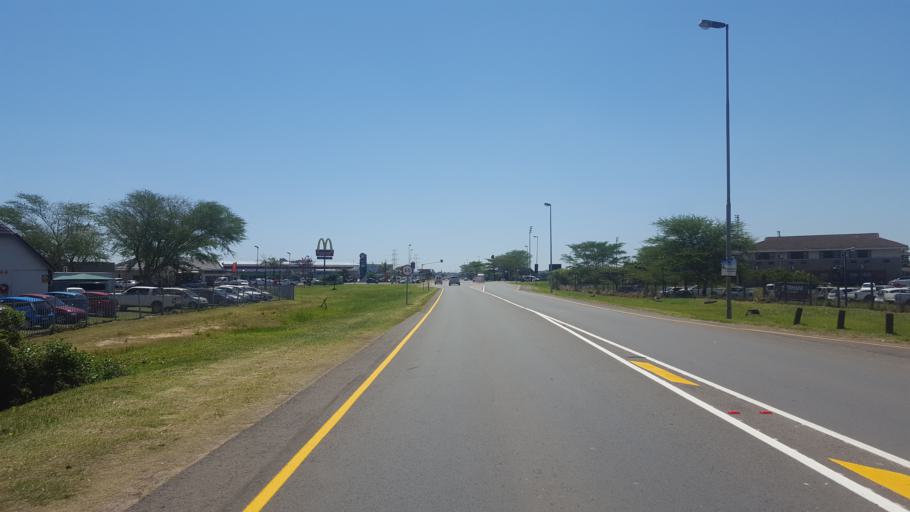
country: ZA
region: KwaZulu-Natal
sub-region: uThungulu District Municipality
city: Richards Bay
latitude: -28.7495
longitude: 32.0545
